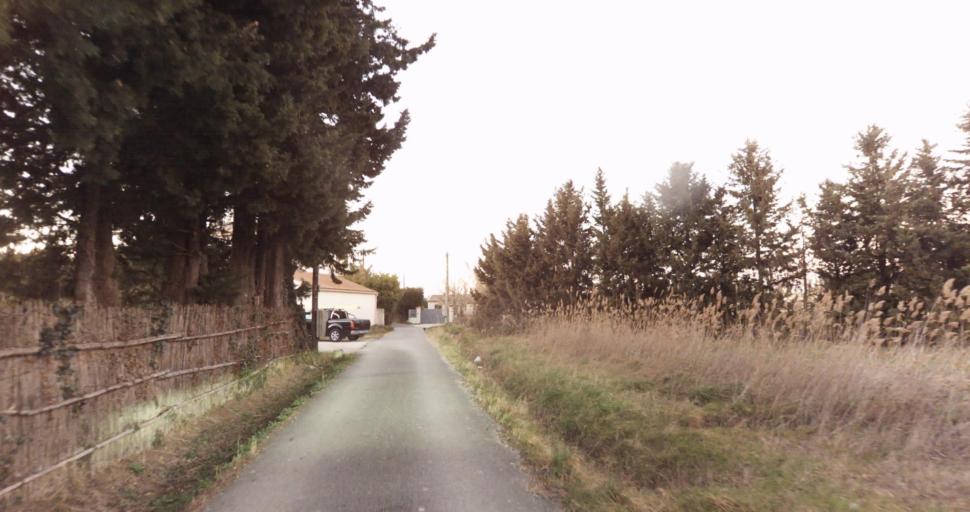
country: FR
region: Provence-Alpes-Cote d'Azur
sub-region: Departement des Bouches-du-Rhone
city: Rognonas
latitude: 43.9109
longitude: 4.7827
